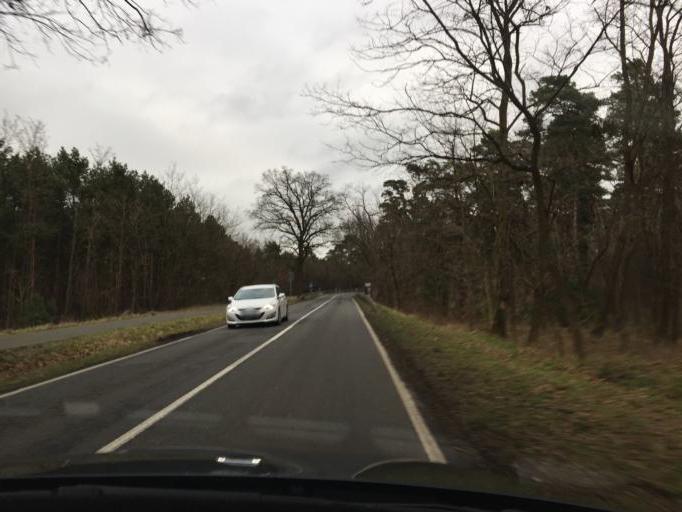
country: DE
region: Brandenburg
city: Mixdorf
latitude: 52.0838
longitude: 14.4879
